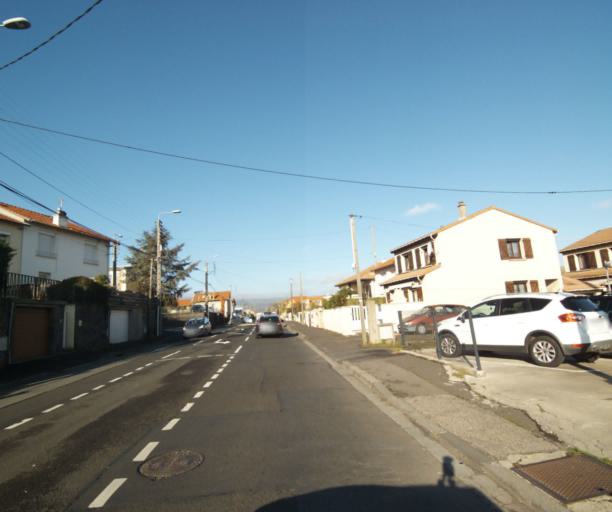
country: FR
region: Auvergne
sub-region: Departement du Puy-de-Dome
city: Aubiere
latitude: 45.7677
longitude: 3.1192
